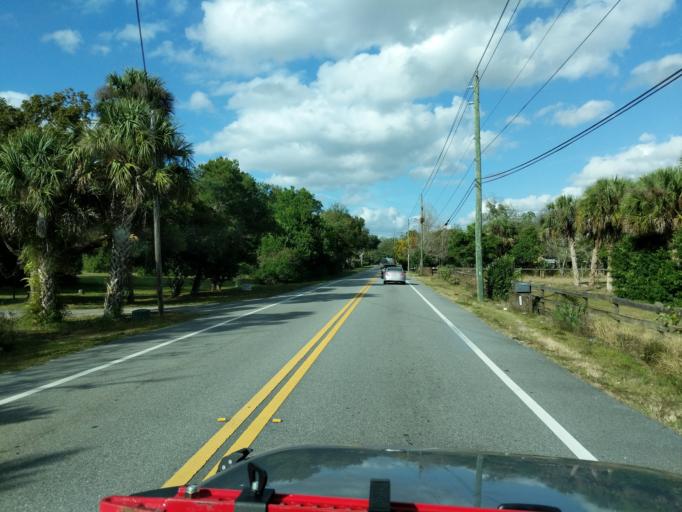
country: US
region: Florida
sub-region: Seminole County
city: Geneva
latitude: 28.7242
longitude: -81.1149
